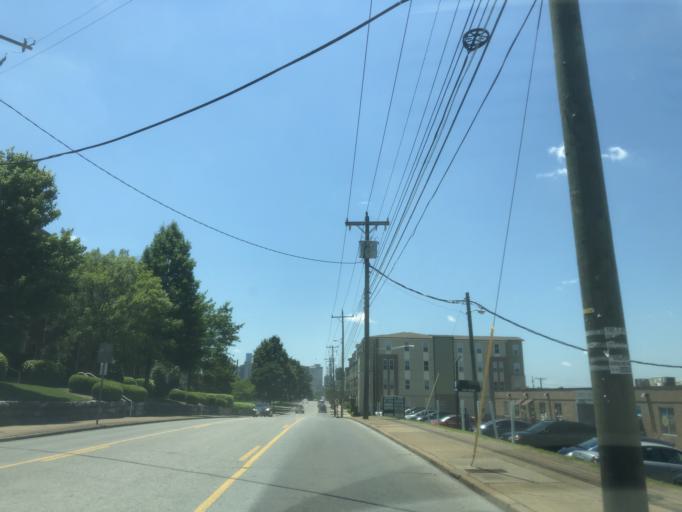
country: US
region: Tennessee
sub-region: Davidson County
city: Nashville
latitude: 36.1746
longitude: -86.7575
